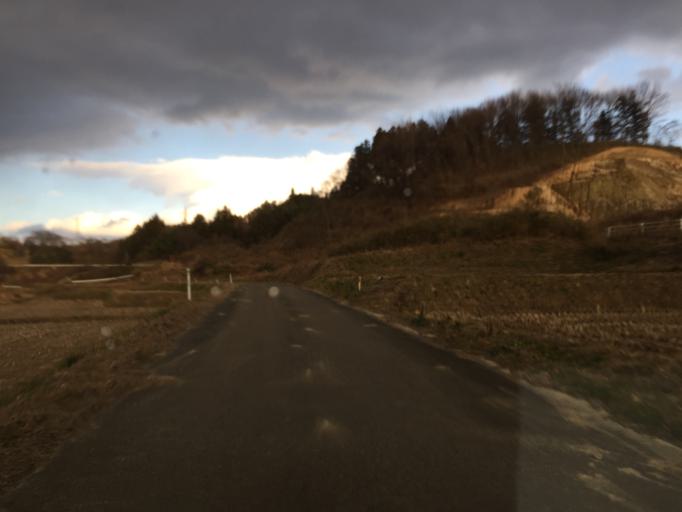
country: JP
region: Fukushima
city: Nihommatsu
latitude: 37.5543
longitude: 140.4384
